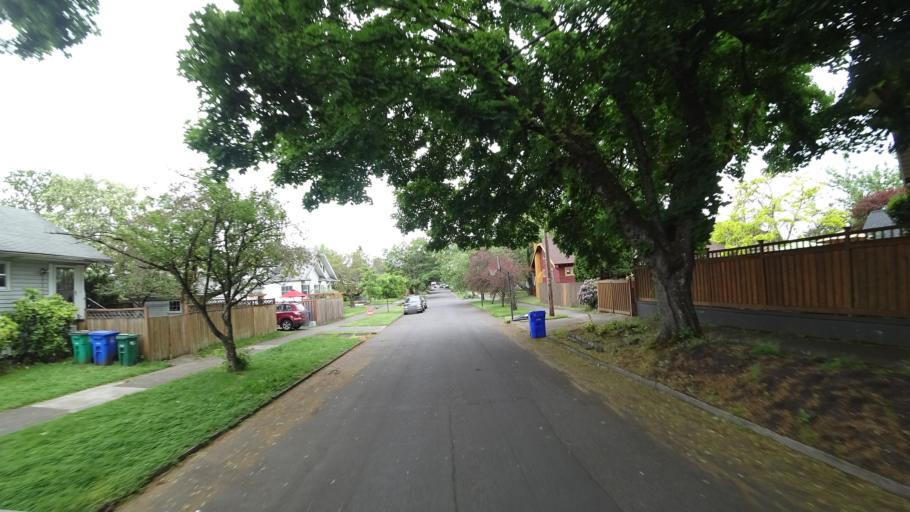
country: US
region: Oregon
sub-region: Multnomah County
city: Portland
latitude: 45.5455
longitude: -122.6150
